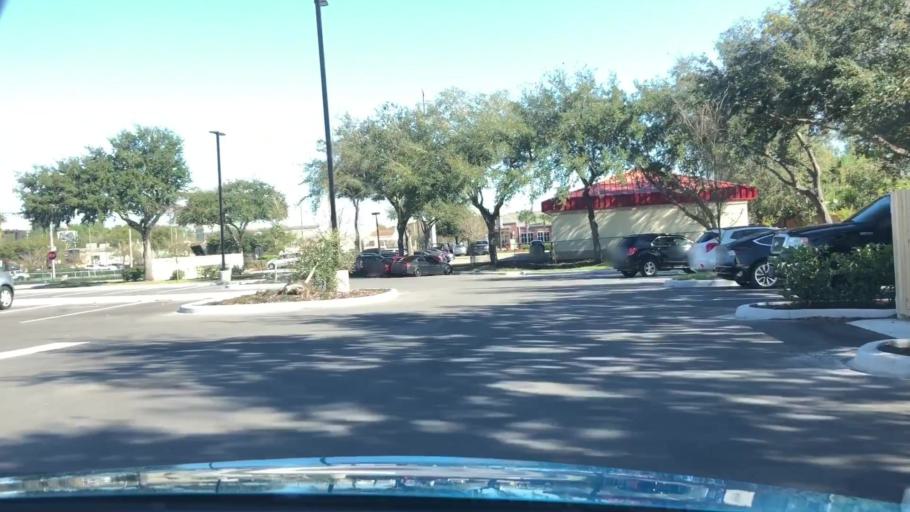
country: US
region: Florida
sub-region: Orange County
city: Conway
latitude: 28.4788
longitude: -81.3320
